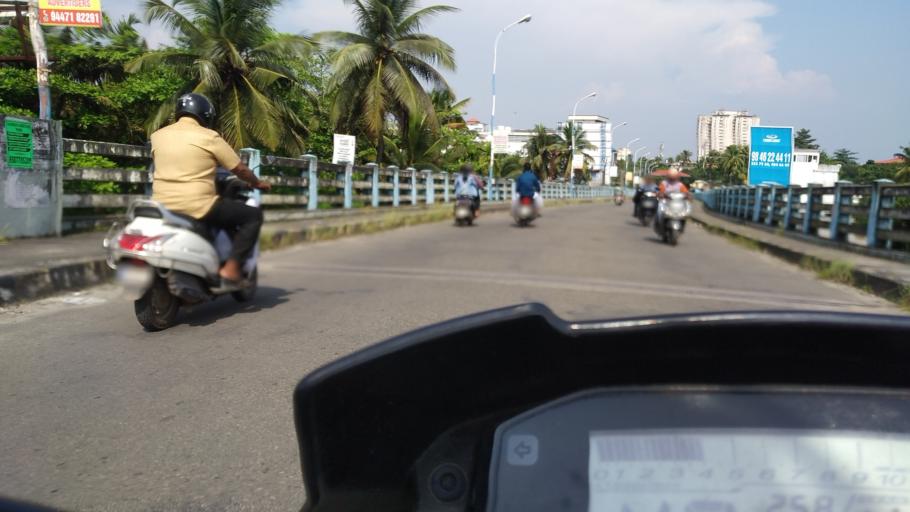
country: IN
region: Kerala
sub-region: Ernakulam
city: Cochin
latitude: 9.9828
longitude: 76.2888
